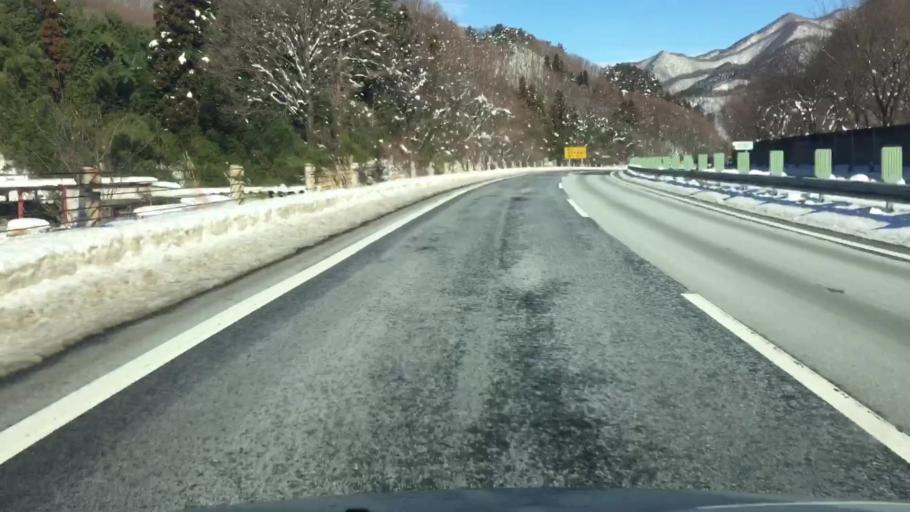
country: JP
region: Gunma
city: Numata
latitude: 36.7362
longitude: 138.9750
